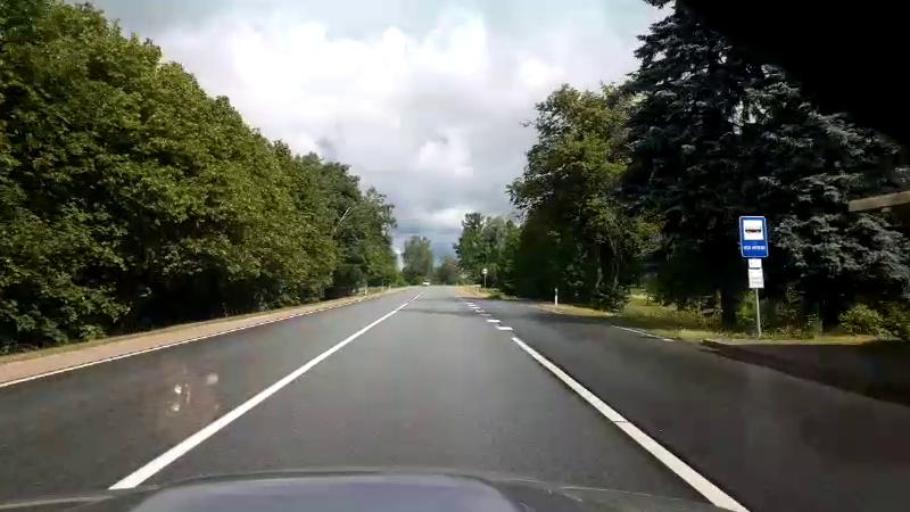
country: LV
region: Lecava
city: Iecava
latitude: 56.5276
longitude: 24.1706
